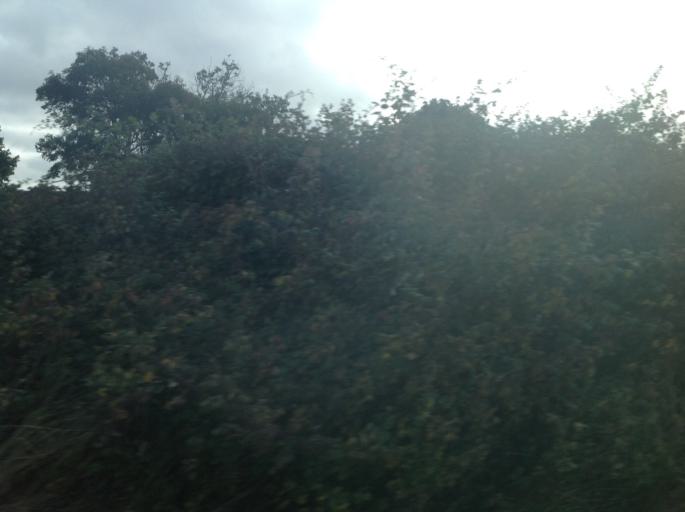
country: GB
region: England
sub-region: Suffolk
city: Felixstowe
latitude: 51.9759
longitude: 1.3386
